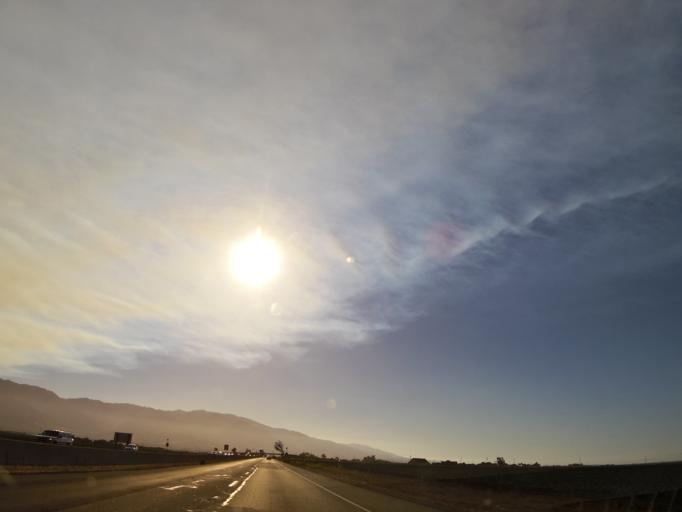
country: US
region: California
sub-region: Monterey County
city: Gonzales
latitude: 36.5220
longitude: -121.4513
